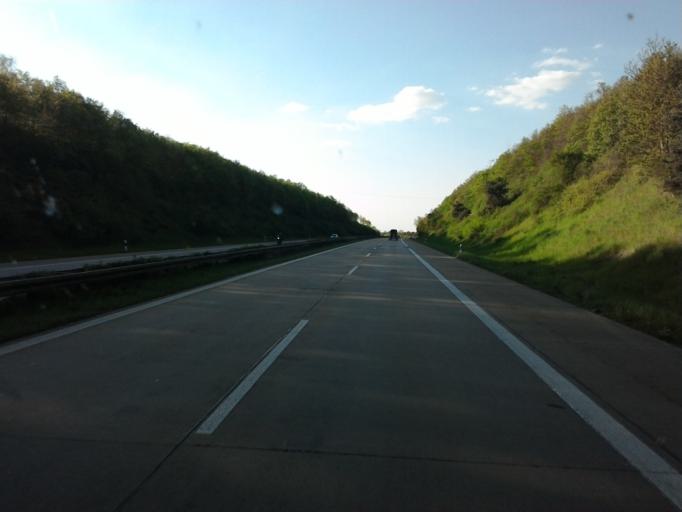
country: DE
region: Bavaria
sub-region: Regierungsbezirk Mittelfranken
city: Diebach
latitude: 49.3098
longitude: 10.2072
